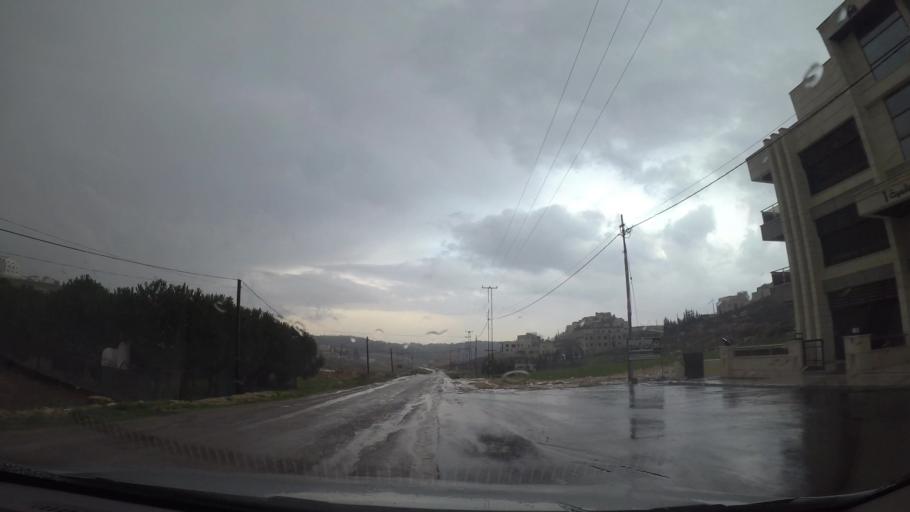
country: JO
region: Amman
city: Umm as Summaq
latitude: 31.8754
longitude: 35.8688
